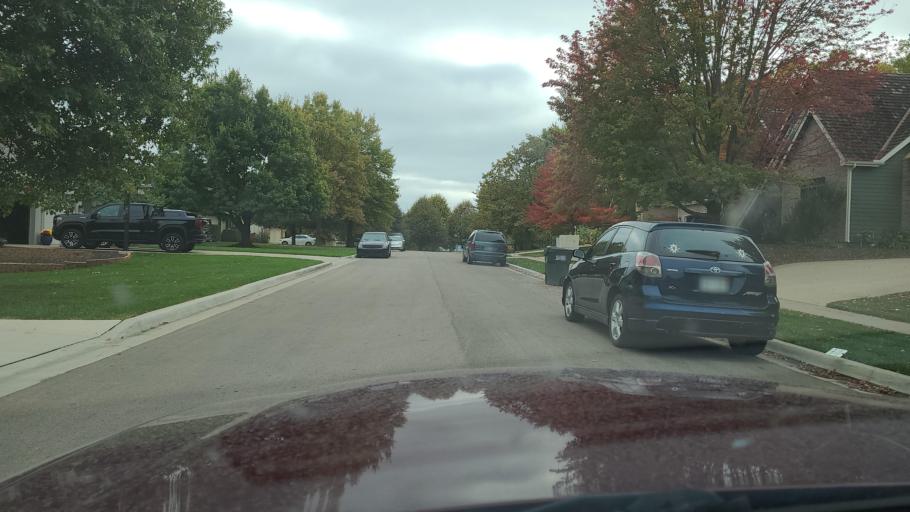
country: US
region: Kansas
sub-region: Douglas County
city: Lawrence
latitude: 38.9703
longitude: -95.3144
